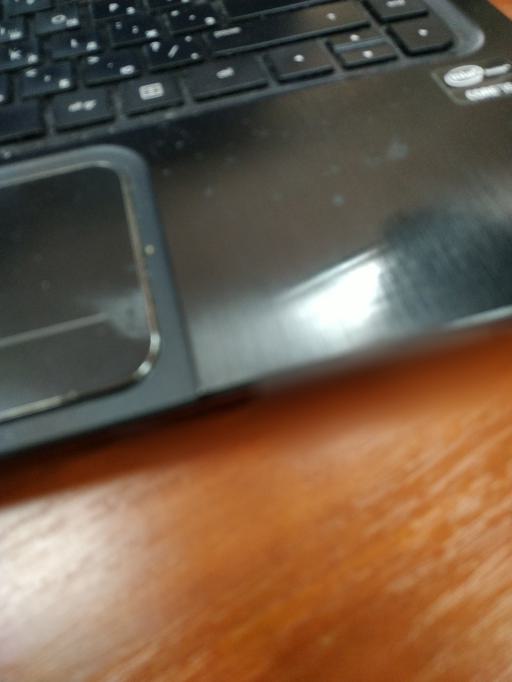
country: RU
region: Moscow
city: Vagonoremont
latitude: 55.9094
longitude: 37.5514
